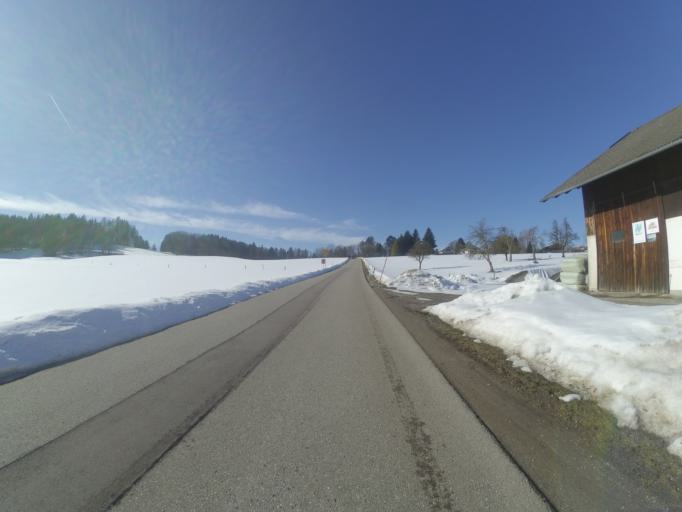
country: DE
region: Bavaria
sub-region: Upper Bavaria
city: Feldkirchen-Westerham
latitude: 47.9129
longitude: 11.8172
